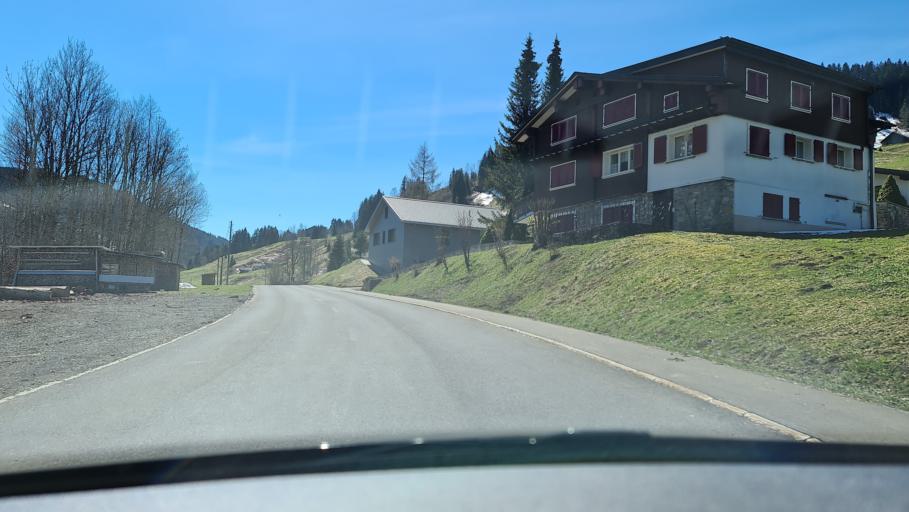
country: CH
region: Schwyz
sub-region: Bezirk Einsiedeln
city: Einsiedeln
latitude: 47.0883
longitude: 8.7222
